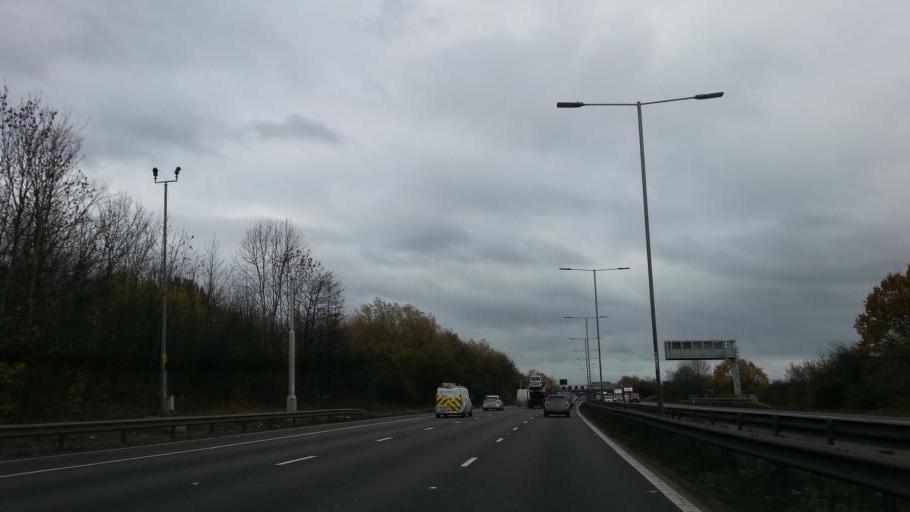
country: GB
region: England
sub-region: Solihull
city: Chelmsley Wood
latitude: 52.4934
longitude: -1.7343
